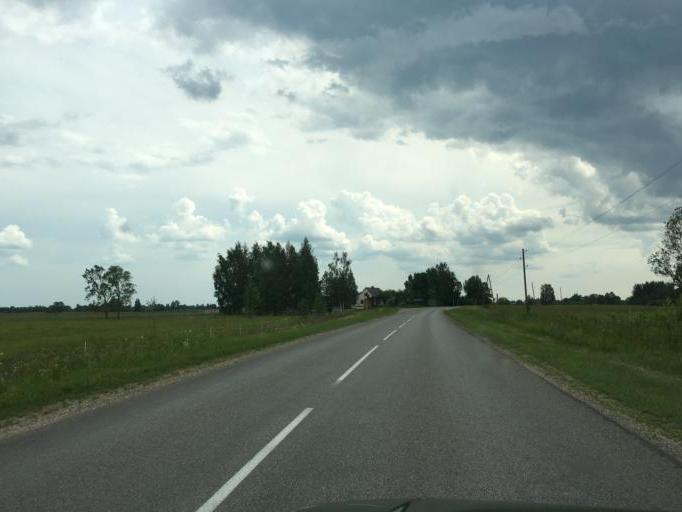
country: LV
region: Rugaju
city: Rugaji
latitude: 56.9200
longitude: 27.0715
